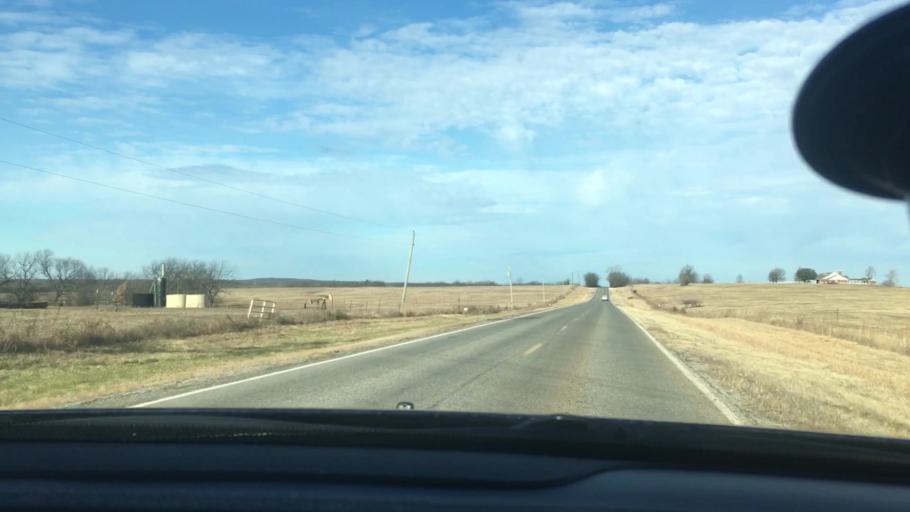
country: US
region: Oklahoma
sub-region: Seminole County
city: Konawa
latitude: 34.9750
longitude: -96.7833
